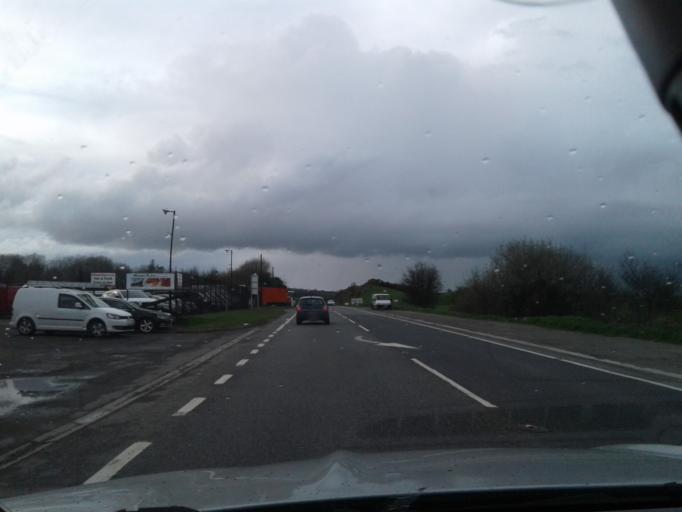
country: GB
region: Northern Ireland
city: Newtownstewart
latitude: 54.7333
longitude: -7.4220
